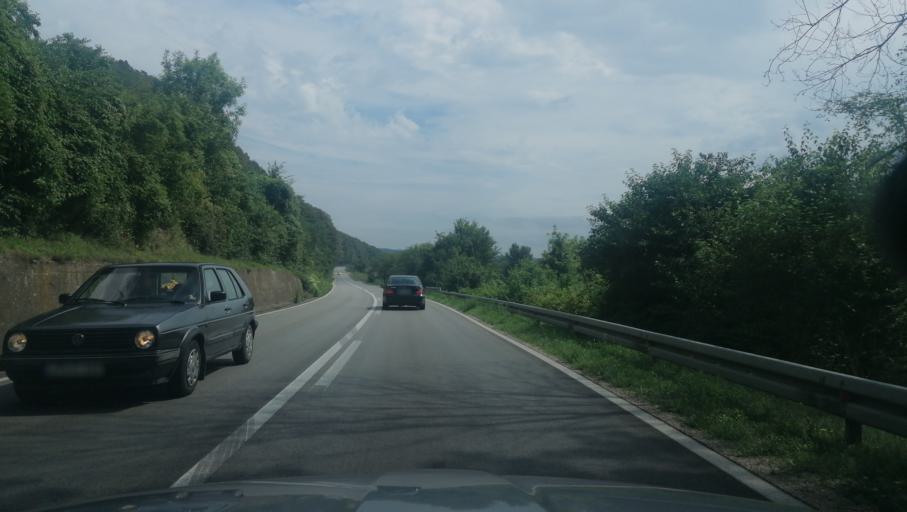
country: BA
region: Federation of Bosnia and Herzegovina
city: Lukavica
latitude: 44.9273
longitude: 18.1698
